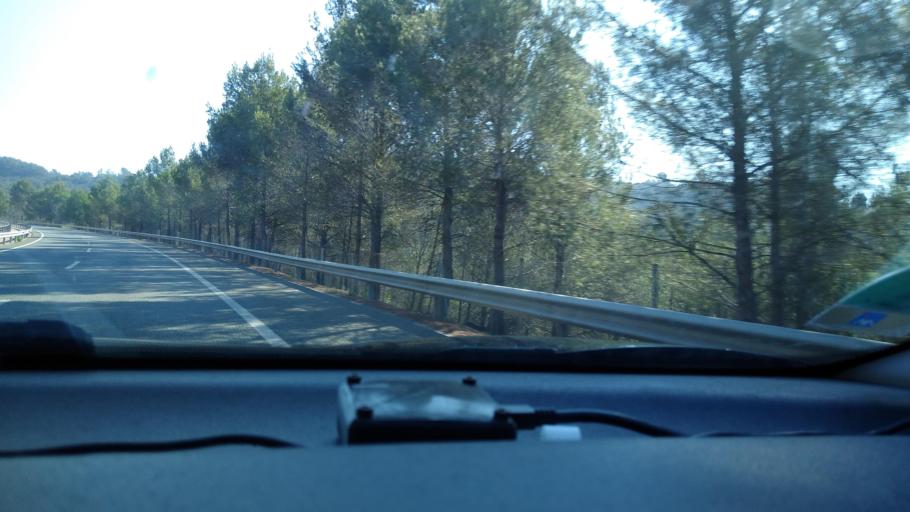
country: ES
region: Catalonia
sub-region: Provincia de Barcelona
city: Viladecavalls
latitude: 41.5695
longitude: 1.9238
